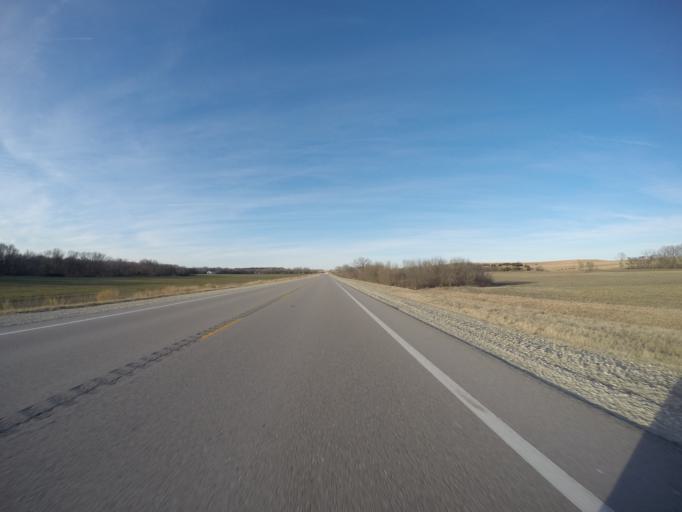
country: US
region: Kansas
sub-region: Marion County
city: Marion
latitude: 38.2675
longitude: -96.9601
